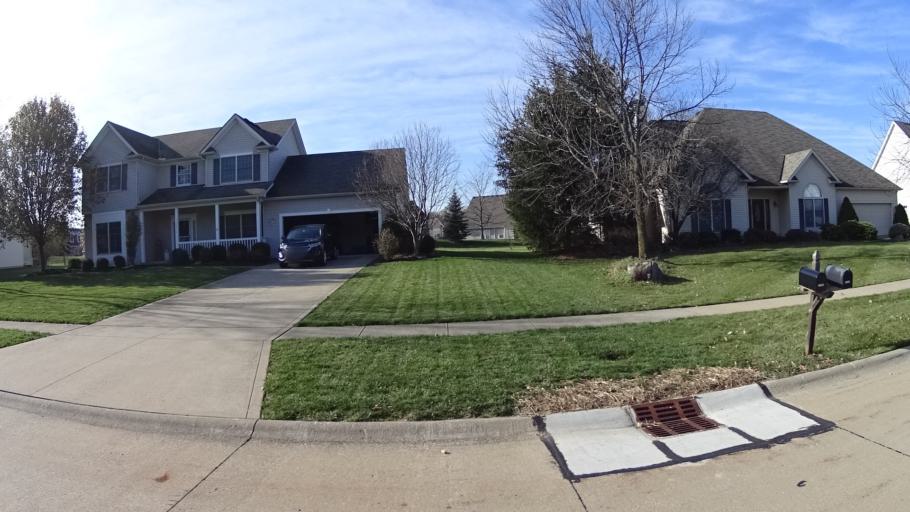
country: US
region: Ohio
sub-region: Lorain County
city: Avon
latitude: 41.4477
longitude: -82.0440
